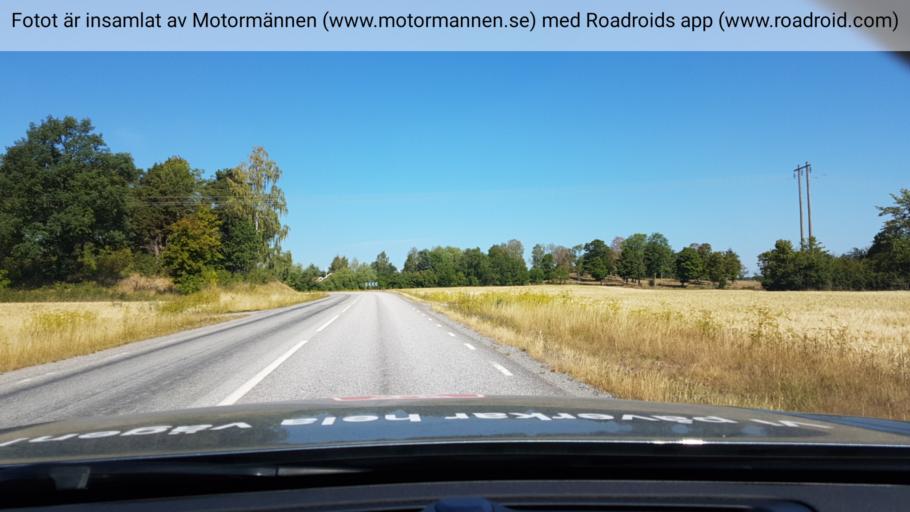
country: SE
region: Stockholm
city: Stenhamra
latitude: 59.3959
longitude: 17.5691
